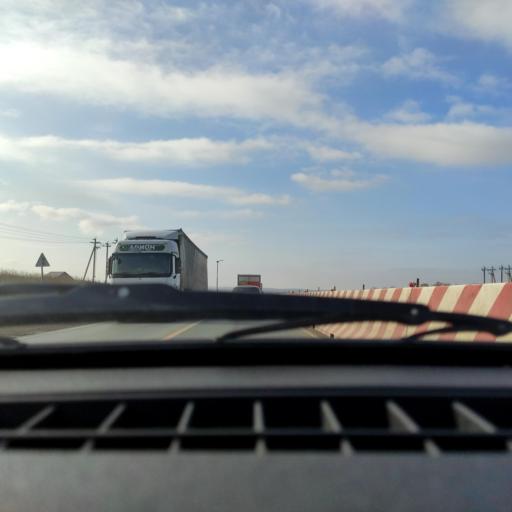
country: RU
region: Bashkortostan
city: Kabakovo
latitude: 54.6781
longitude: 56.1888
